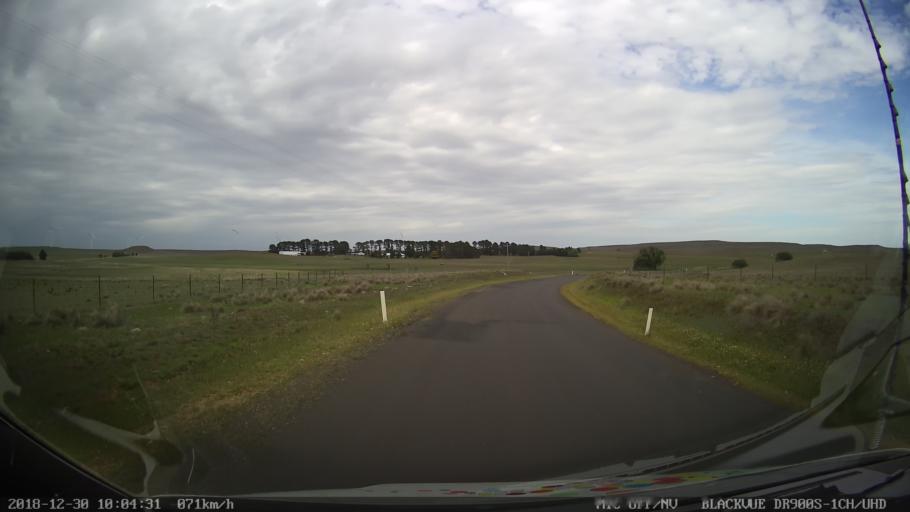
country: AU
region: New South Wales
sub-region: Cooma-Monaro
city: Cooma
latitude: -36.5224
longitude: 149.1456
